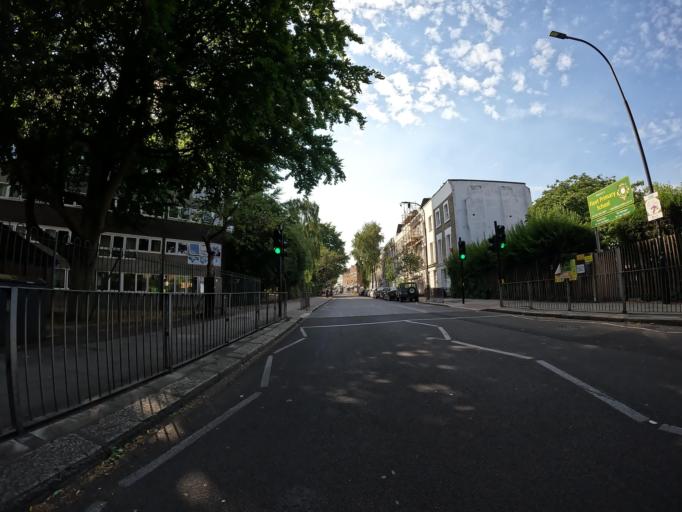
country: GB
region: England
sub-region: Greater London
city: Belsize Park
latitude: 51.5705
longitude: -0.1775
